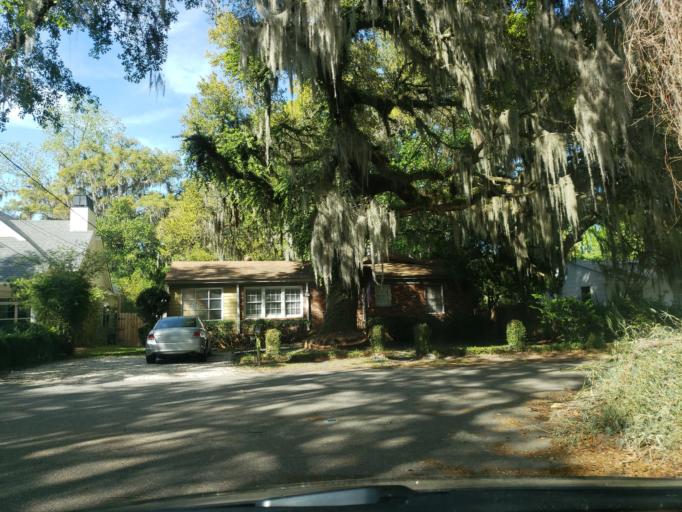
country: US
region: Georgia
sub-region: Chatham County
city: Isle of Hope
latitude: 31.9794
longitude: -81.0601
